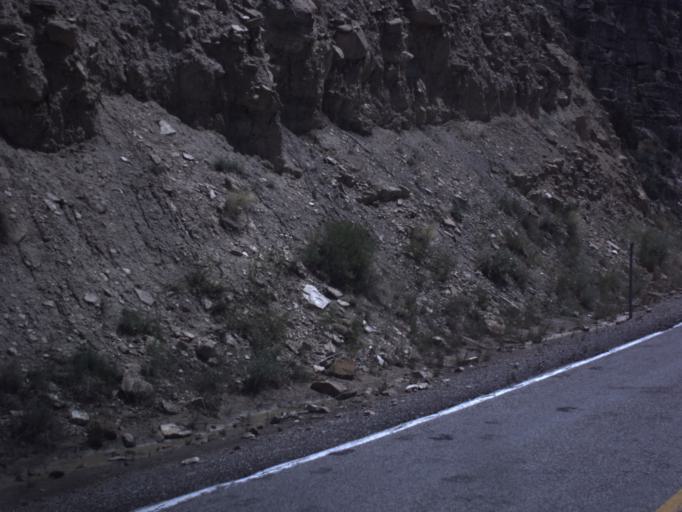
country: US
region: Utah
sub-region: Emery County
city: Orangeville
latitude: 39.2963
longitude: -111.2718
